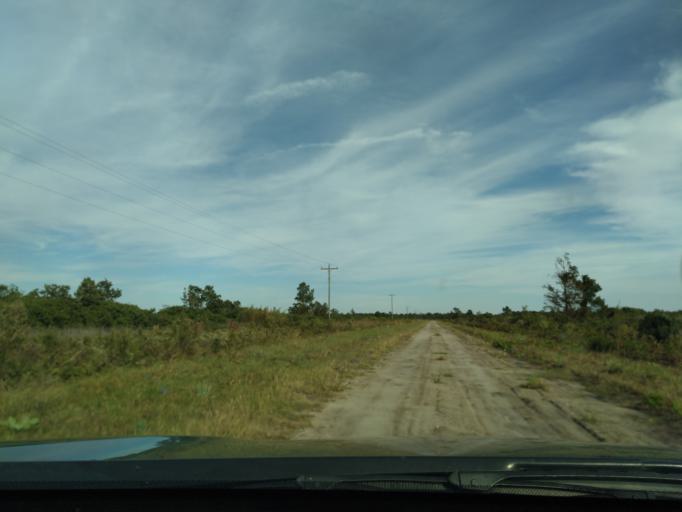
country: US
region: North Carolina
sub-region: Beaufort County
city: Belhaven
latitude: 35.6899
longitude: -76.5334
